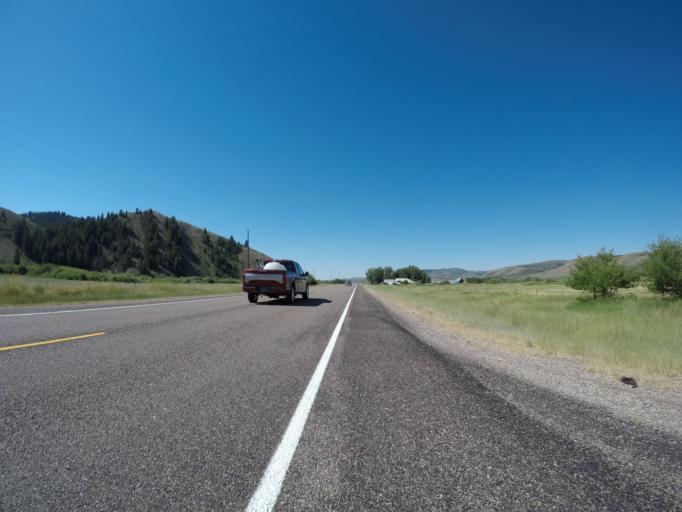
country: US
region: Idaho
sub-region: Bear Lake County
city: Montpelier
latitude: 42.3946
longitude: -111.0507
